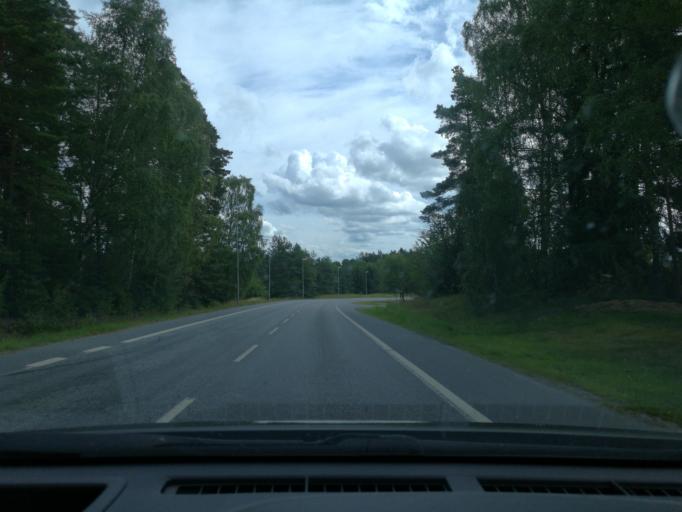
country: SE
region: Stockholm
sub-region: Sigtuna Kommun
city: Marsta
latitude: 59.6394
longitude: 17.8475
